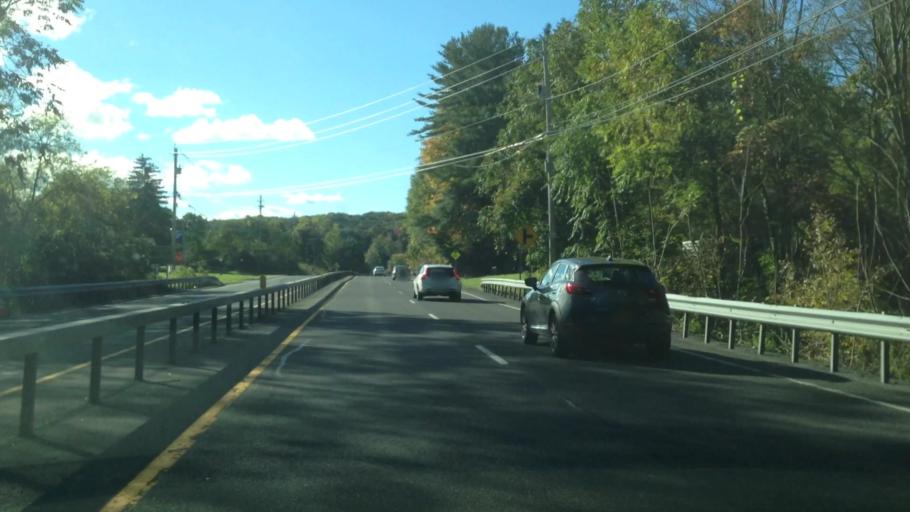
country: US
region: New York
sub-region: Ulster County
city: Highland
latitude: 41.7256
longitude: -73.9613
